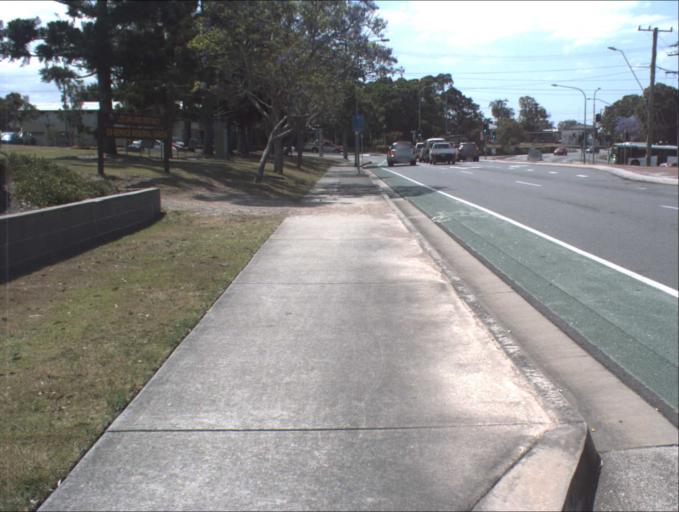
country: AU
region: Queensland
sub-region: Logan
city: Logan City
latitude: -27.6426
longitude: 153.1054
